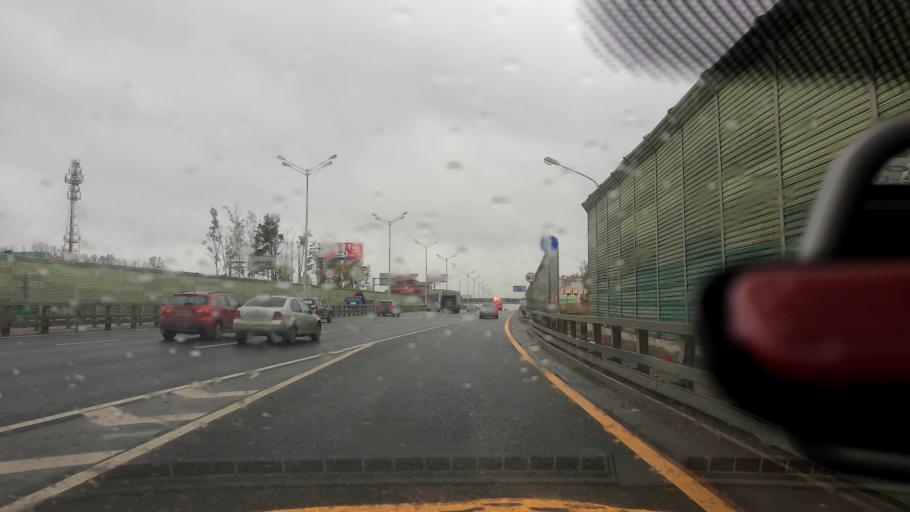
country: RU
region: Moskovskaya
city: Lesnoy Gorodok
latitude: 55.6397
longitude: 37.2281
